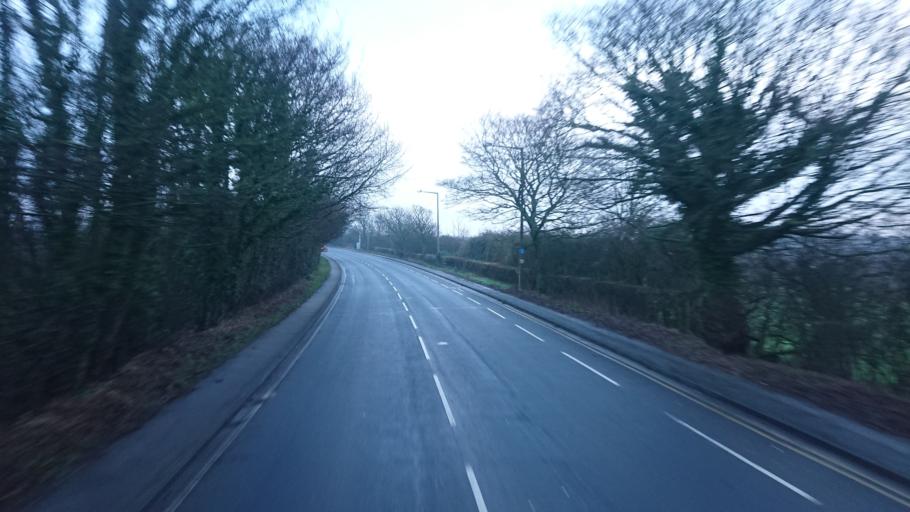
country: GB
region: England
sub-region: Lancashire
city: Bolton le Sands
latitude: 54.0862
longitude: -2.8229
